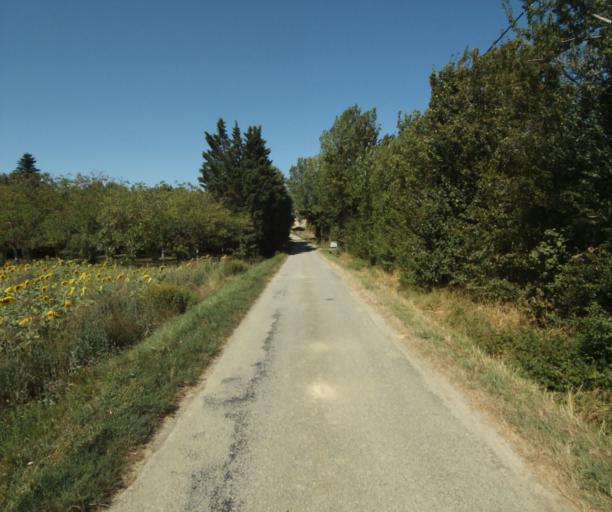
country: FR
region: Midi-Pyrenees
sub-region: Departement de la Haute-Garonne
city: Saint-Felix-Lauragais
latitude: 43.4824
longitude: 1.8975
